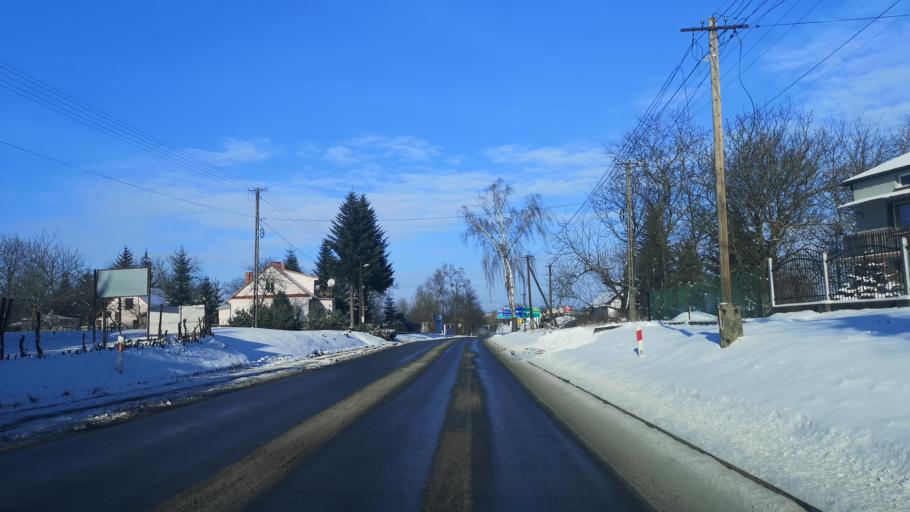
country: PL
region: Subcarpathian Voivodeship
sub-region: Powiat przeworski
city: Gorliczyna
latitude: 50.0943
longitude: 22.4921
